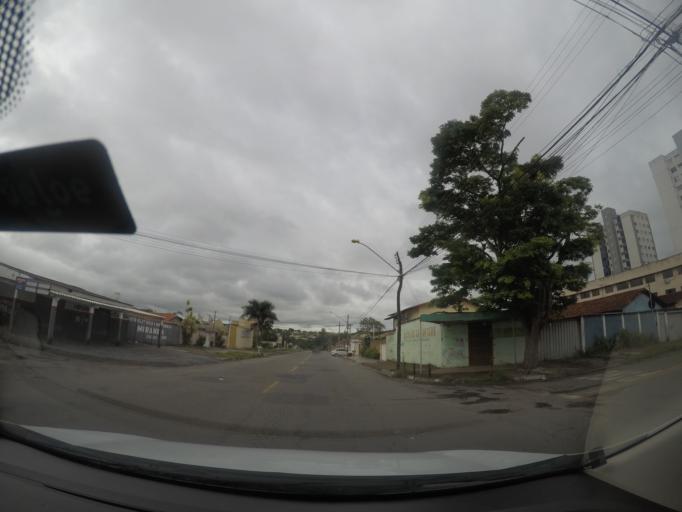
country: BR
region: Goias
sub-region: Goiania
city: Goiania
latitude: -16.7217
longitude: -49.2909
